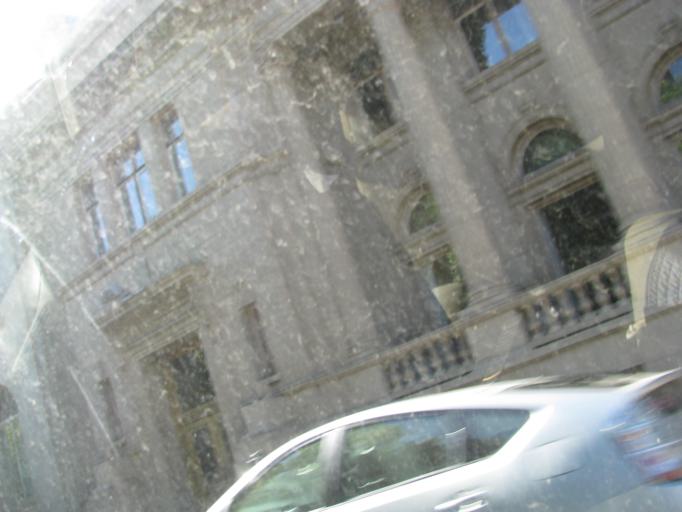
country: US
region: Washington
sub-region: Spokane County
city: Spokane
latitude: 47.6586
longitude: -117.4282
